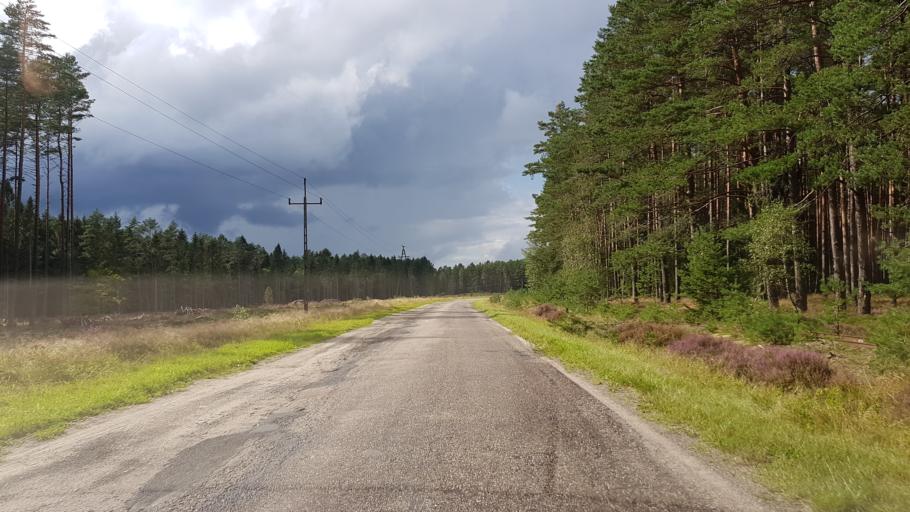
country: PL
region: West Pomeranian Voivodeship
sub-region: Powiat bialogardzki
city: Tychowo
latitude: 54.0410
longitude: 16.3244
